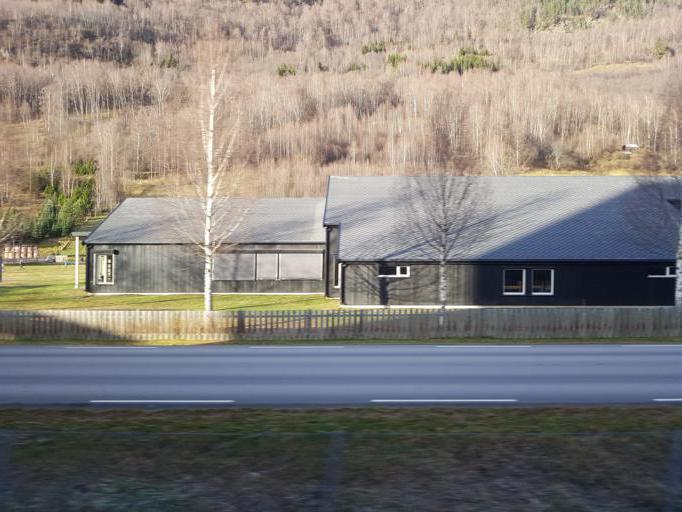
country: NO
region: Oppland
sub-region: Sel
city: Otta
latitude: 61.7913
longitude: 9.5471
